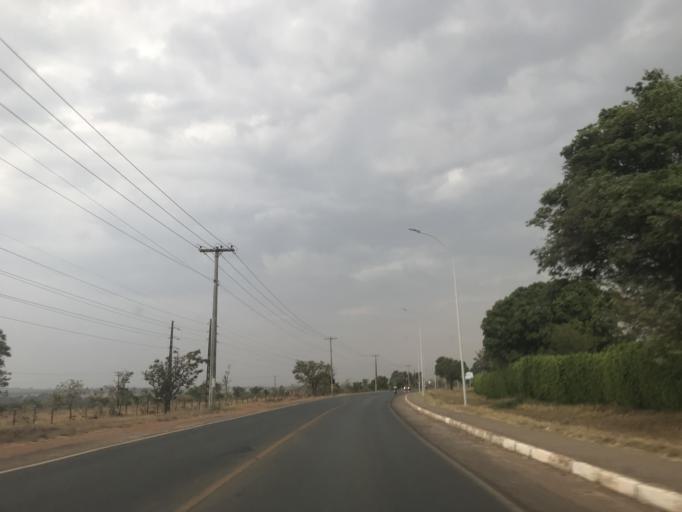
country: BR
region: Federal District
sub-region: Brasilia
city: Brasilia
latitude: -15.6652
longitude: -47.8204
